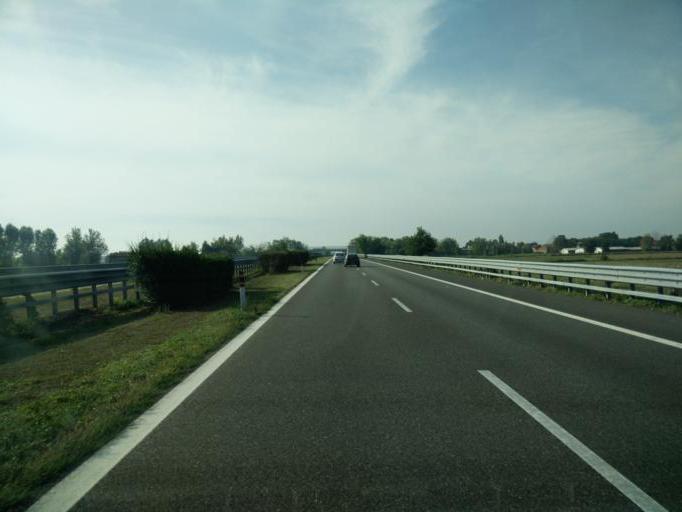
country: IT
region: Lombardy
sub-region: Provincia di Cremona
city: Corte de' Frati
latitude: 45.2112
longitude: 10.1071
